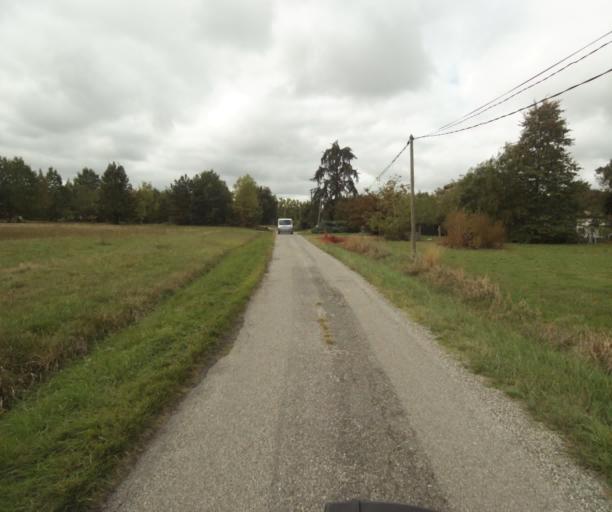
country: FR
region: Midi-Pyrenees
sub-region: Departement du Tarn-et-Garonne
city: Montech
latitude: 43.9714
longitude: 1.2487
